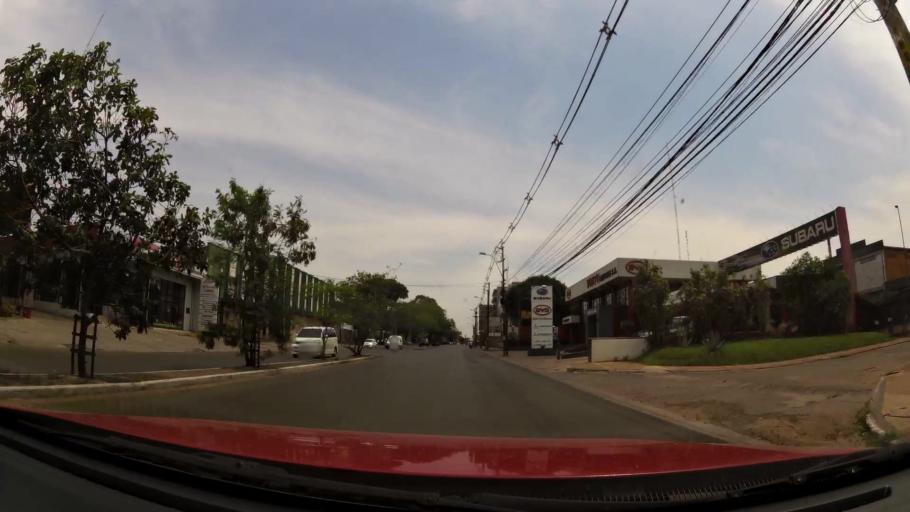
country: PY
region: Central
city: Lambare
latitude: -25.3179
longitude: -57.5690
